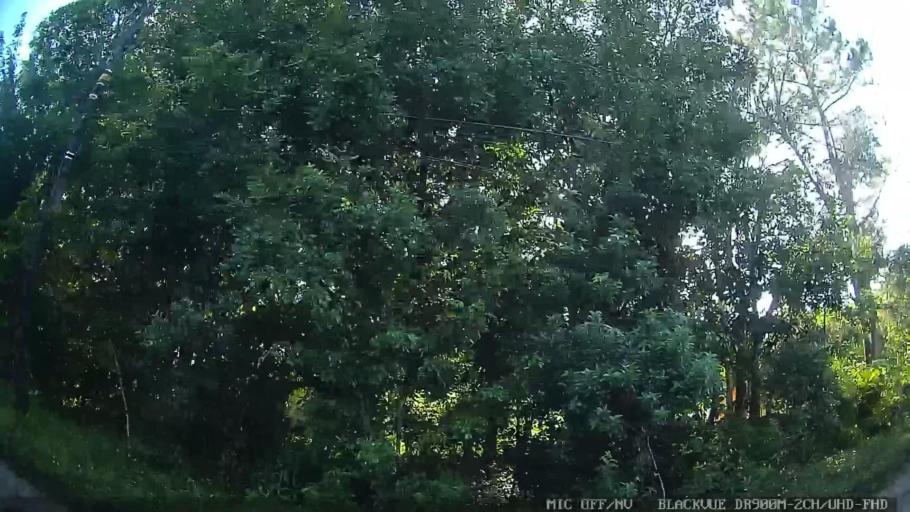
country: BR
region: Sao Paulo
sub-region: Itanhaem
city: Itanhaem
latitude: -24.2027
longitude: -46.8858
